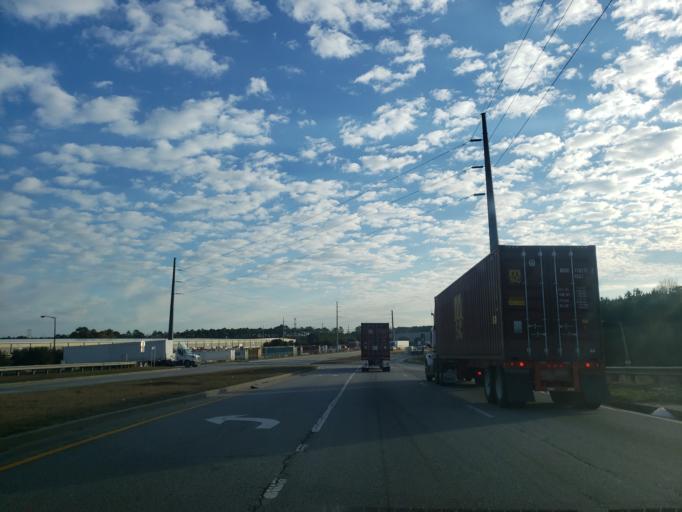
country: US
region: Georgia
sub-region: Chatham County
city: Port Wentworth
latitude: 32.1645
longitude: -81.1983
